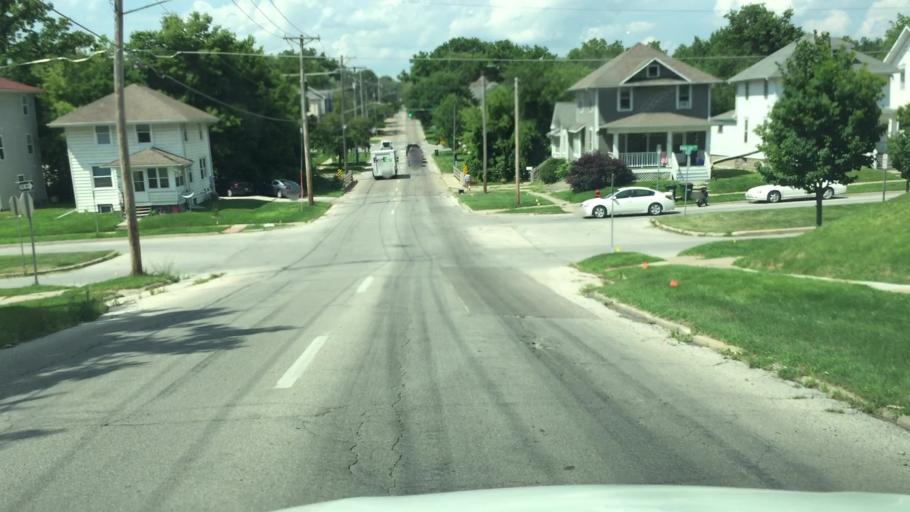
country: US
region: Iowa
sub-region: Johnson County
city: Iowa City
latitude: 41.6609
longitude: -91.5229
